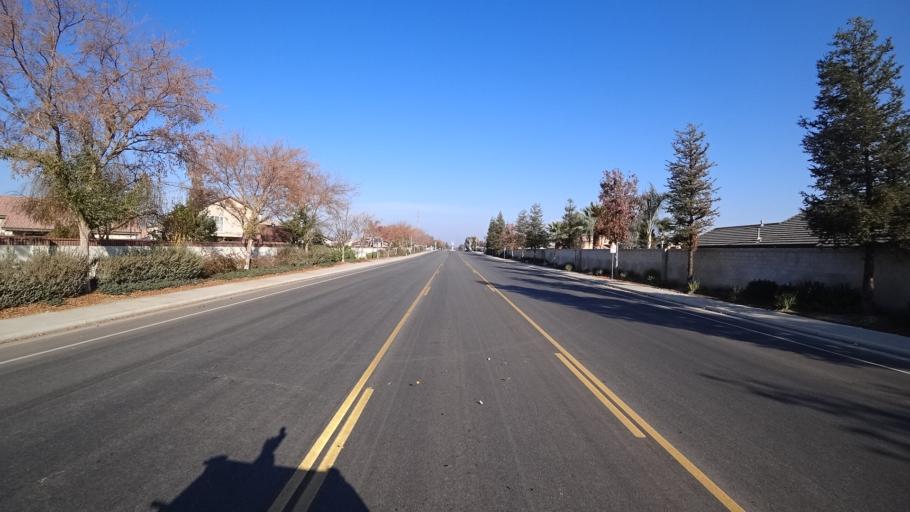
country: US
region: California
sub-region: Kern County
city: Greenacres
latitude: 35.3087
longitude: -119.1188
